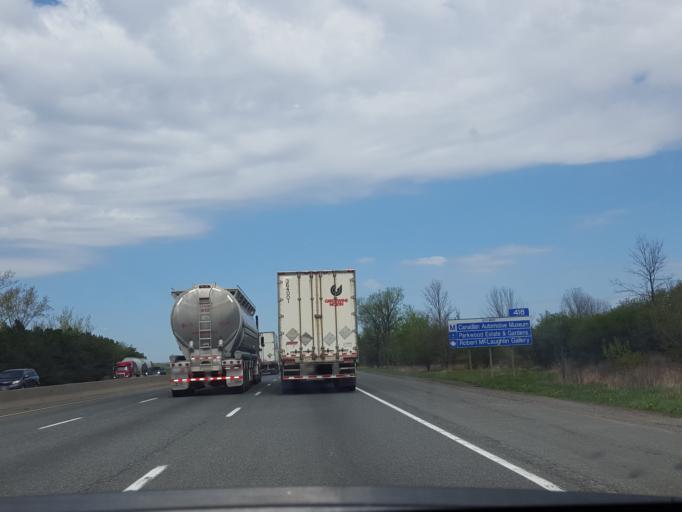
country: CA
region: Ontario
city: Oshawa
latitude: 43.8804
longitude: -78.8053
